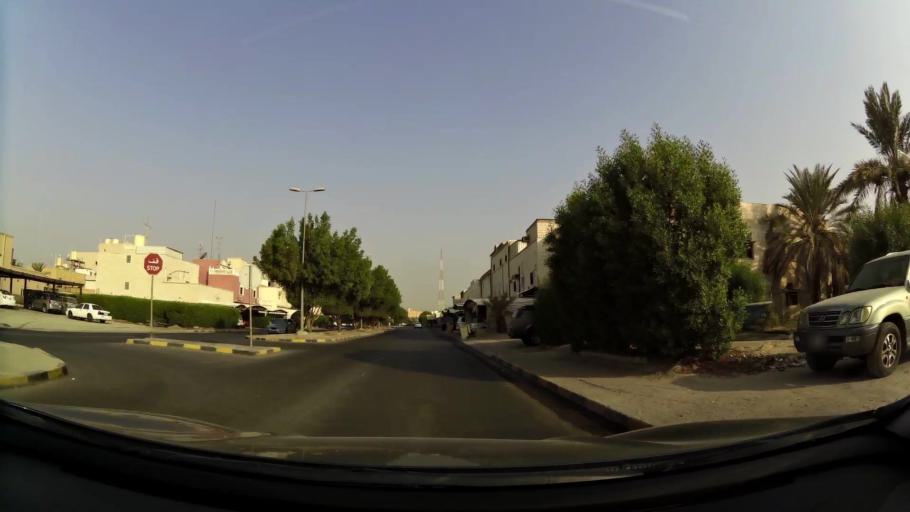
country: KW
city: Bayan
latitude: 29.2936
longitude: 48.0554
